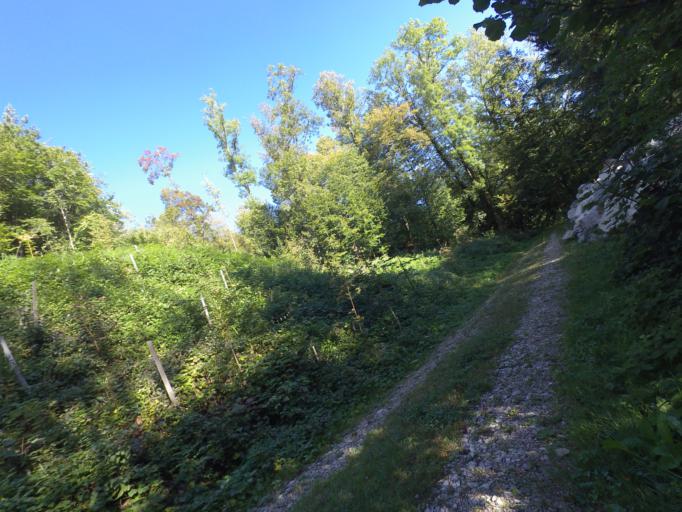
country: AT
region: Salzburg
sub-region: Politischer Bezirk Hallein
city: Oberalm
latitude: 47.6946
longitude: 13.0762
